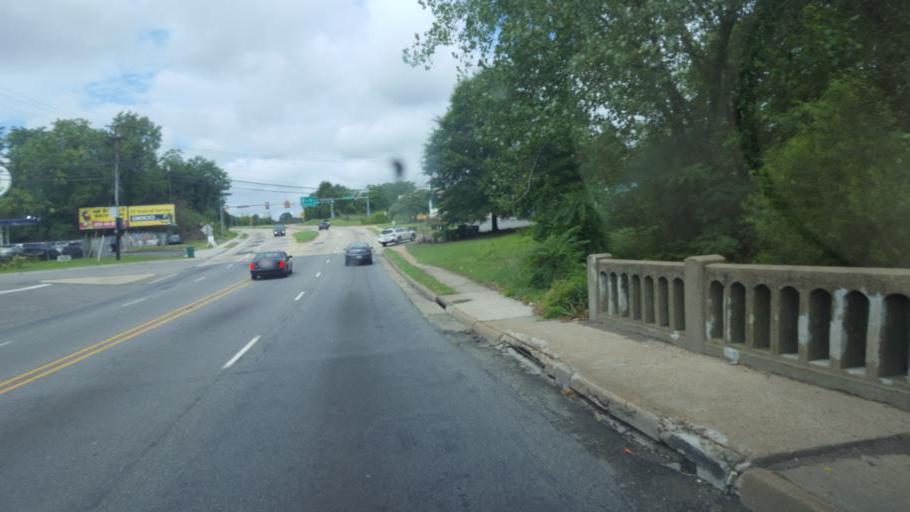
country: US
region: Virginia
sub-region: Henrico County
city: Montrose
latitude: 37.5434
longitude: -77.3883
